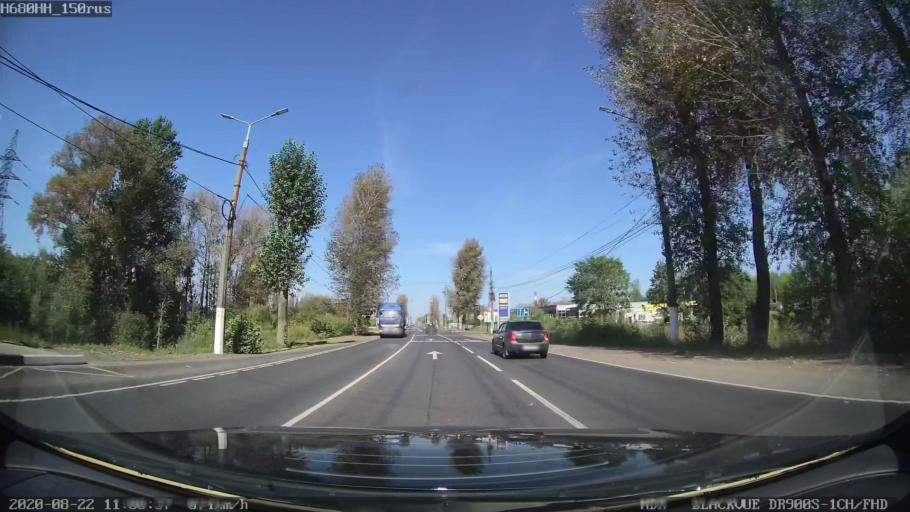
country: RU
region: Tverskaya
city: Tver
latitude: 56.8295
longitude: 35.9705
